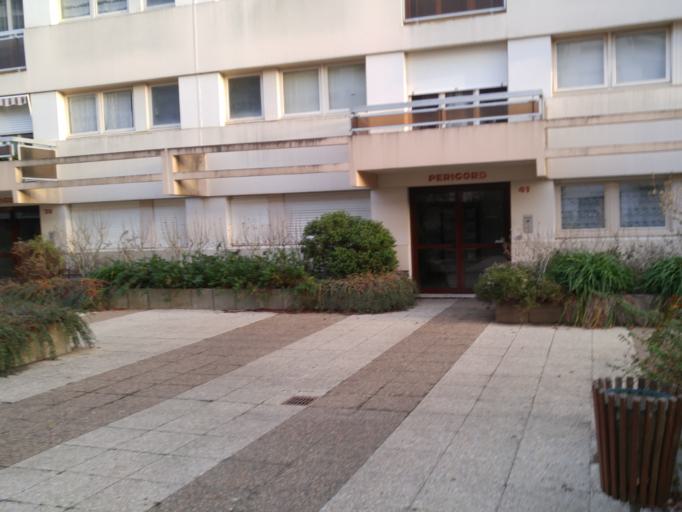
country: FR
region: Pays de la Loire
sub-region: Departement de Maine-et-Loire
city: Angers
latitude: 47.4534
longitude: -0.5560
